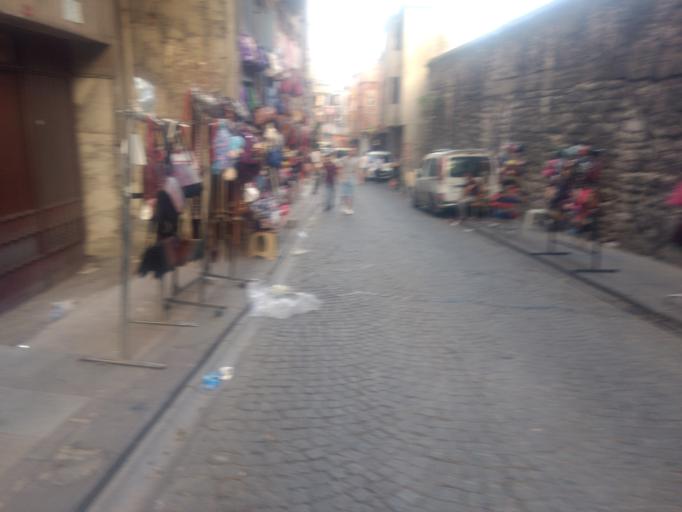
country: TR
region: Istanbul
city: Eminoenue
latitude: 41.0170
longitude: 28.9649
